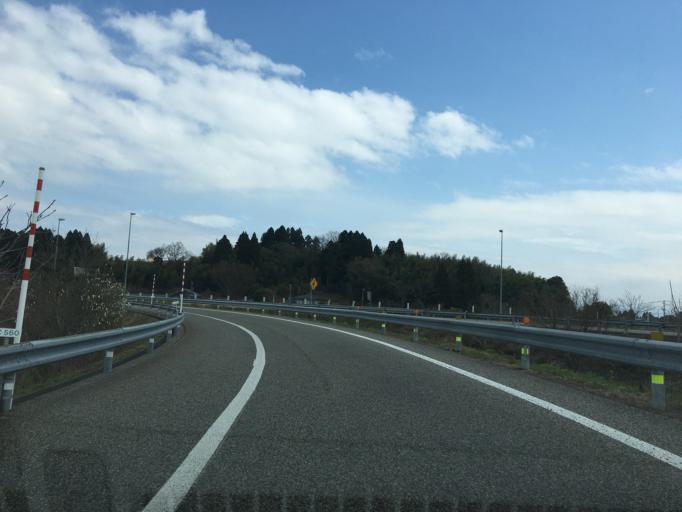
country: JP
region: Toyama
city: Kuragaki-kosugi
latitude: 36.6815
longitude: 137.1340
